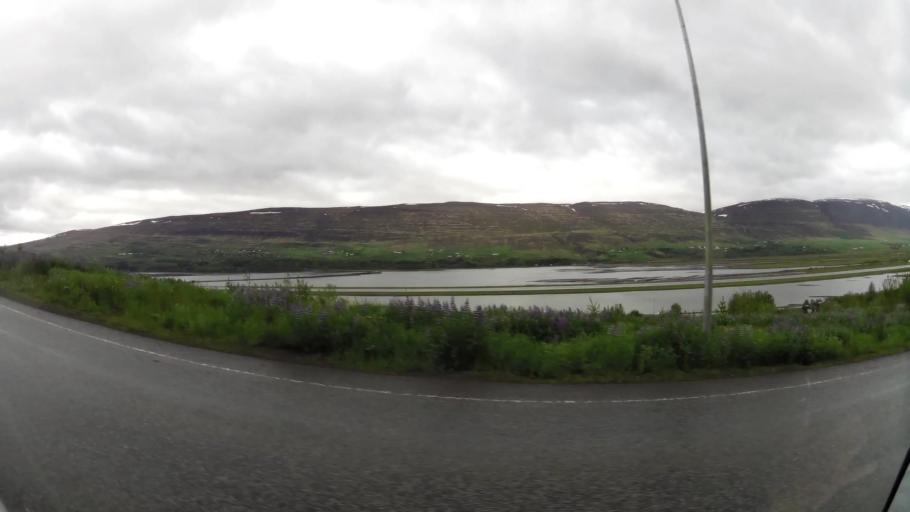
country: IS
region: Northeast
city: Akureyri
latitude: 65.6626
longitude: -18.0858
